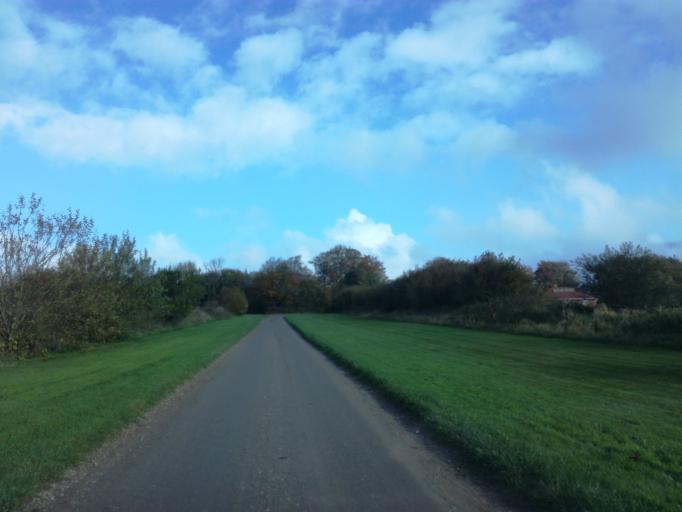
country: DK
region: South Denmark
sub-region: Vejle Kommune
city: Brejning
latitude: 55.6568
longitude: 9.6862
